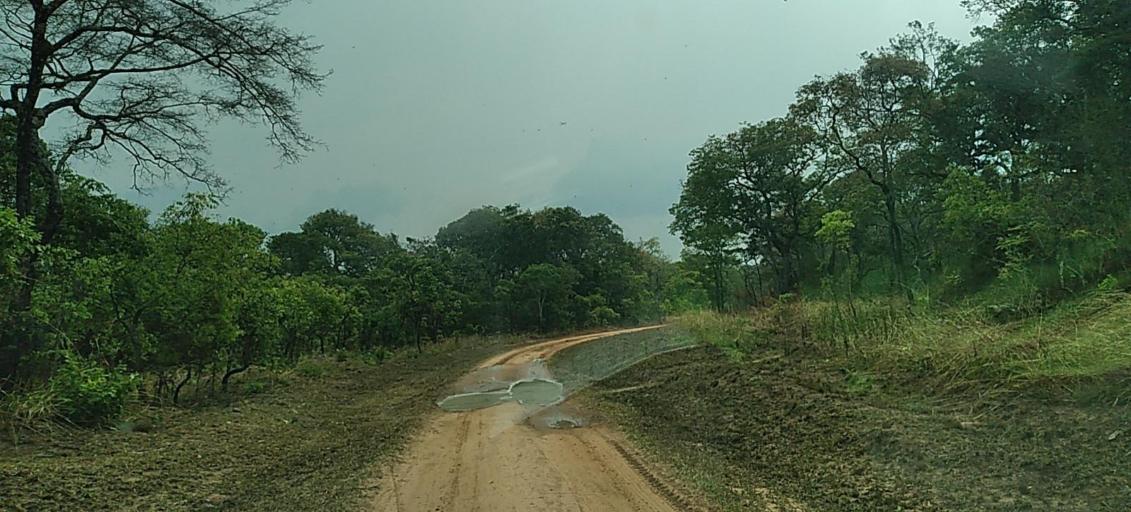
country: ZM
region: North-Western
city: Mwinilunga
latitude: -11.4666
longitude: 24.4757
